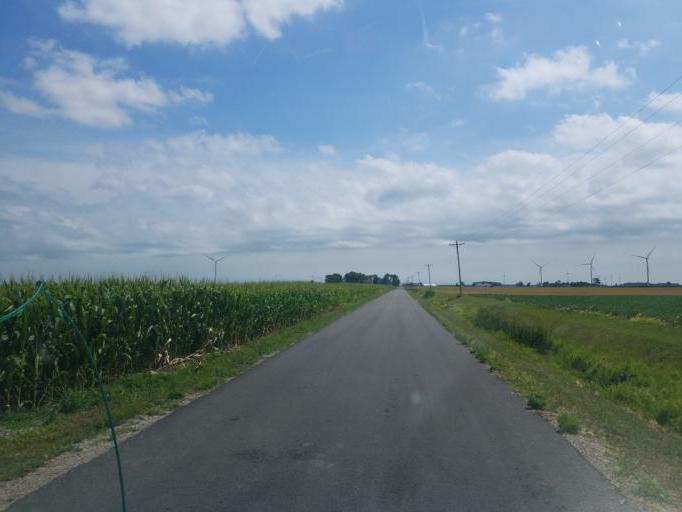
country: US
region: Ohio
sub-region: Paulding County
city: Payne
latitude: 41.1104
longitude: -84.7651
